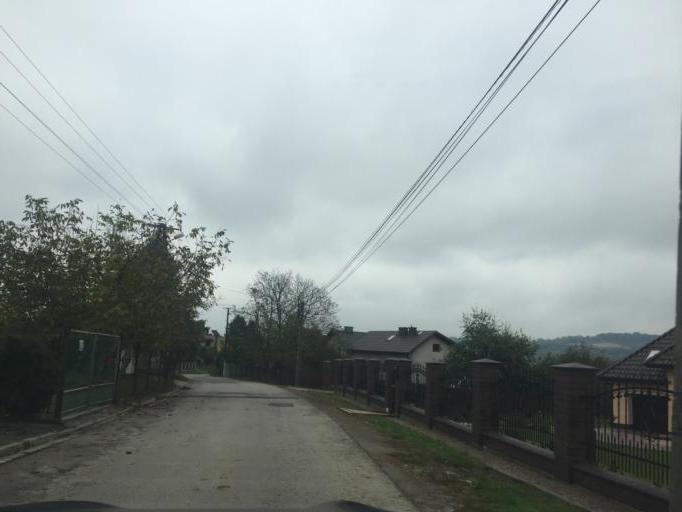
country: PL
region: Lesser Poland Voivodeship
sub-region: Powiat wielicki
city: Wieliczka
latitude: 49.9925
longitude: 20.0254
